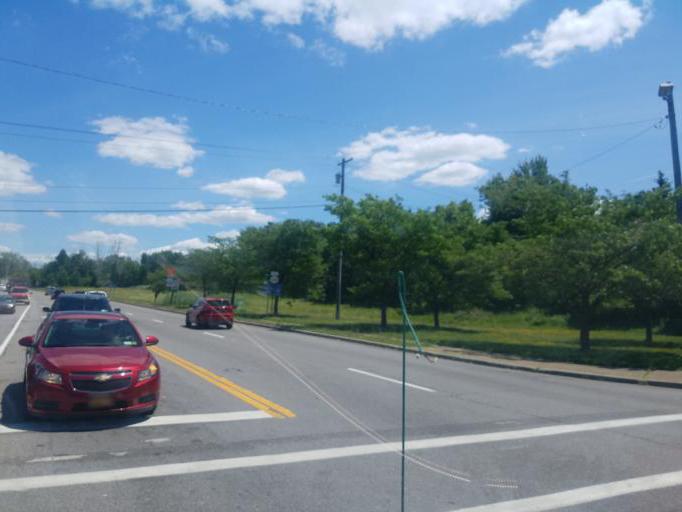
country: US
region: New York
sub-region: Erie County
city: Blasdell
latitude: 42.7892
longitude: -78.8237
